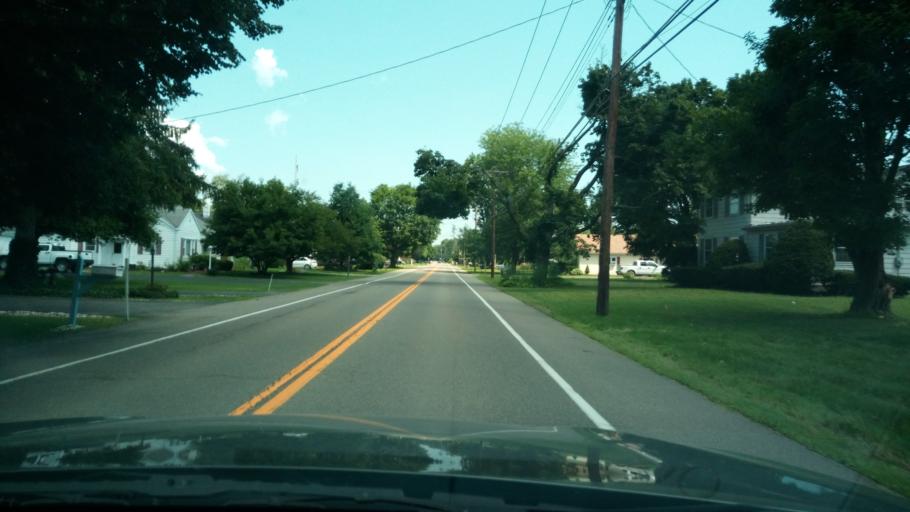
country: US
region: New York
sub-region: Chemung County
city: Horseheads North
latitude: 42.1950
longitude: -76.8135
